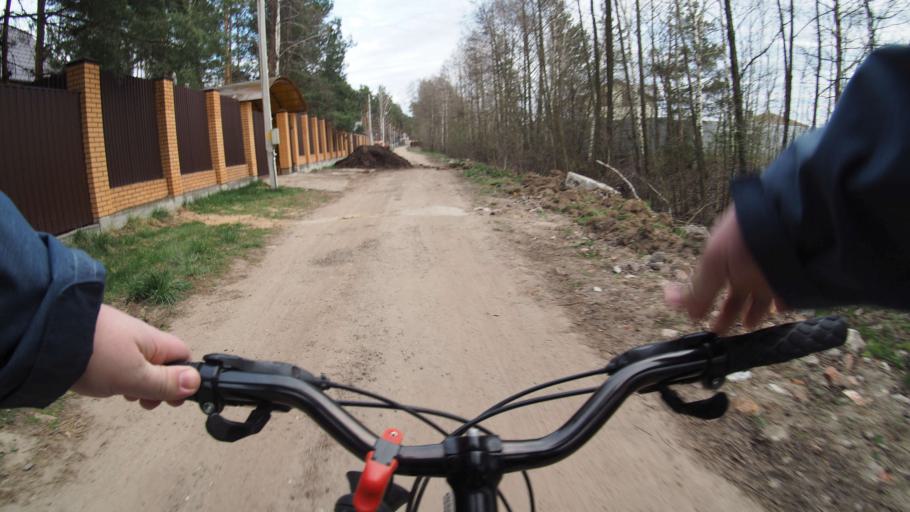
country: RU
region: Moskovskaya
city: Ramenskoye
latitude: 55.5891
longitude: 38.2932
